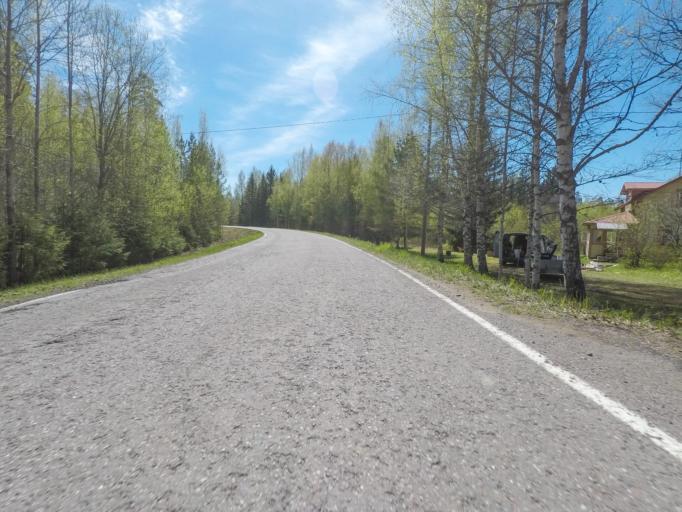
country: FI
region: Uusimaa
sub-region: Helsinki
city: Kaerkoelae
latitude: 60.5888
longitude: 23.7956
